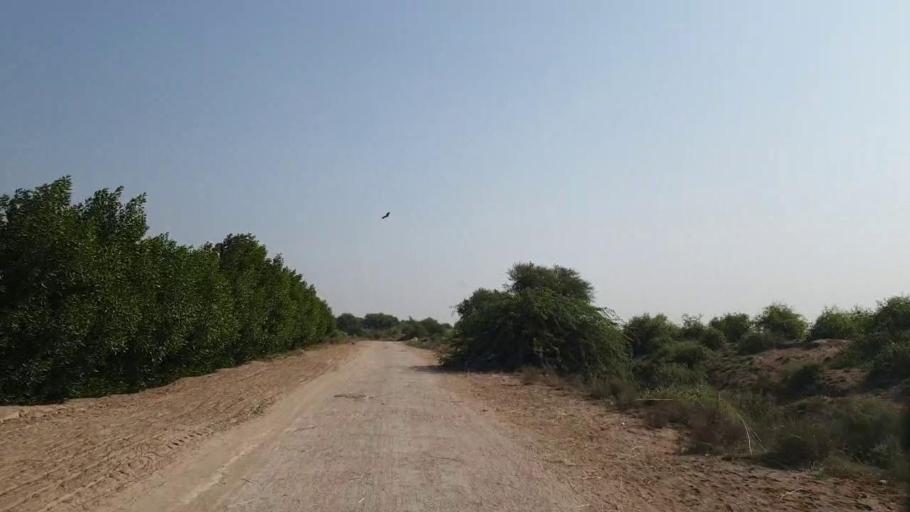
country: PK
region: Sindh
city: Bulri
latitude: 24.9328
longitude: 68.3697
